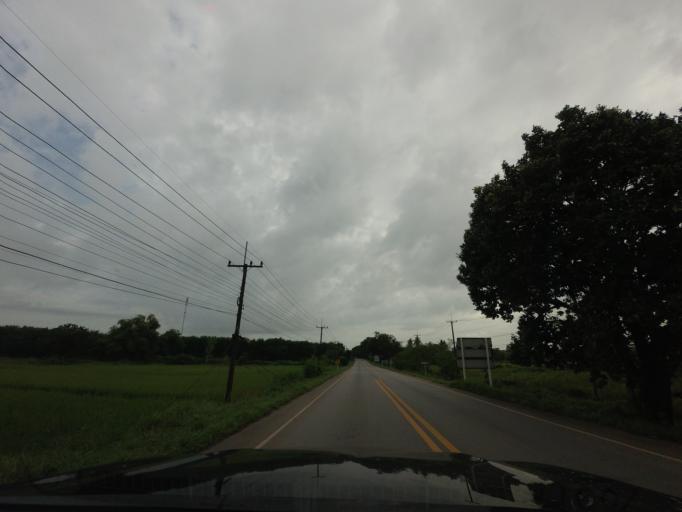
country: TH
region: Changwat Udon Thani
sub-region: Amphoe Ban Phue
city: Ban Phue
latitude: 17.7200
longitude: 102.3923
